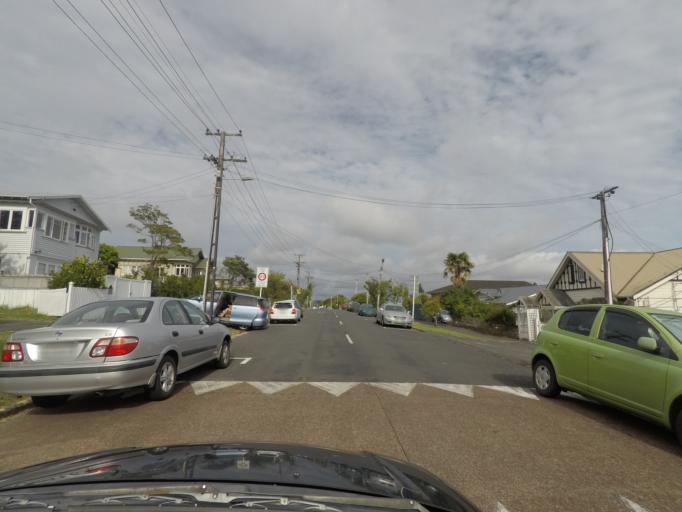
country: NZ
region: Auckland
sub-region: Auckland
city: Rosebank
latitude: -36.8802
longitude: 174.7138
